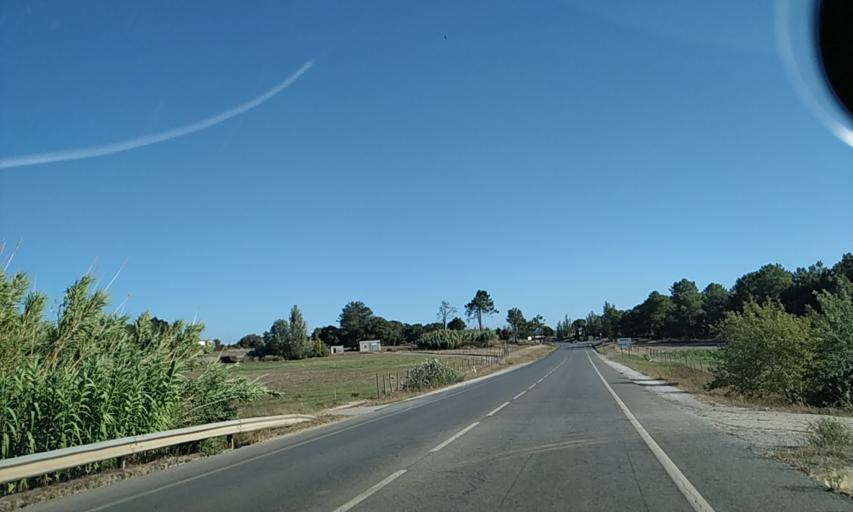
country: PT
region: Setubal
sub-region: Moita
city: Moita
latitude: 38.6380
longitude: -8.9714
